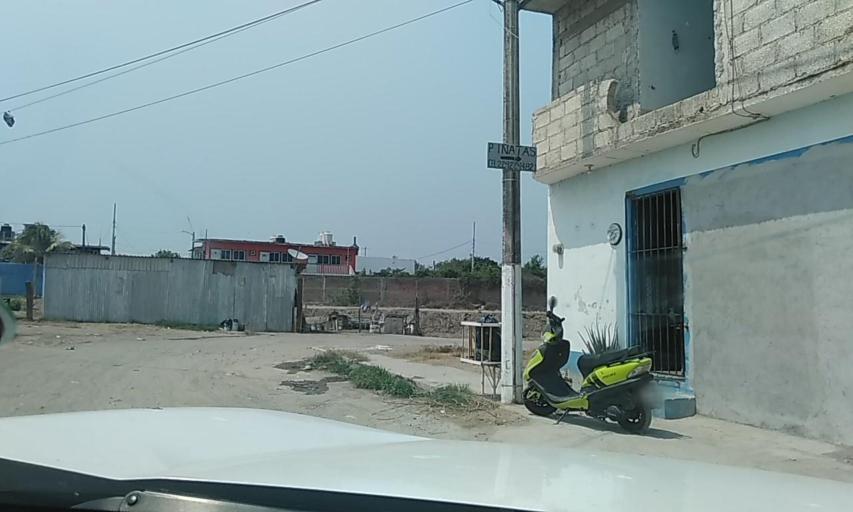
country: MX
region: Veracruz
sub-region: Veracruz
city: Las Amapolas
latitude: 19.1771
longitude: -96.1779
